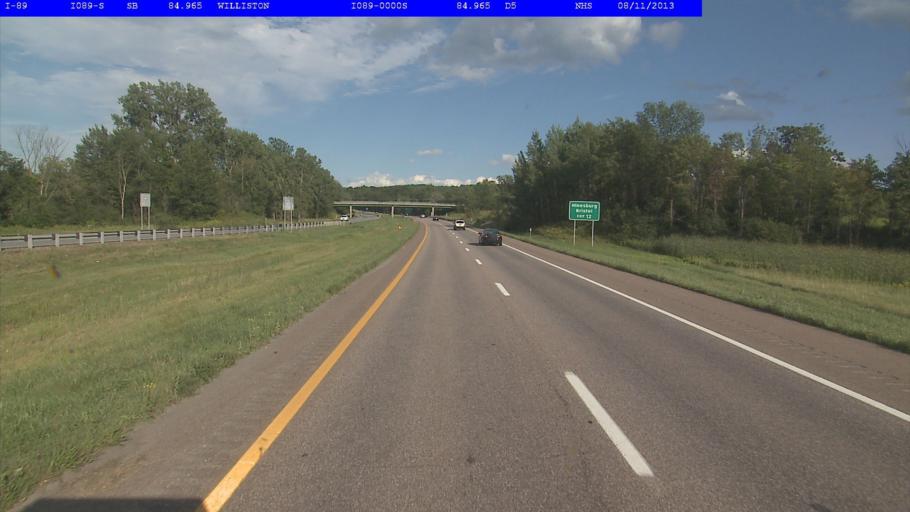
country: US
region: Vermont
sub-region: Chittenden County
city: South Burlington
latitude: 44.4420
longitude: -73.1350
